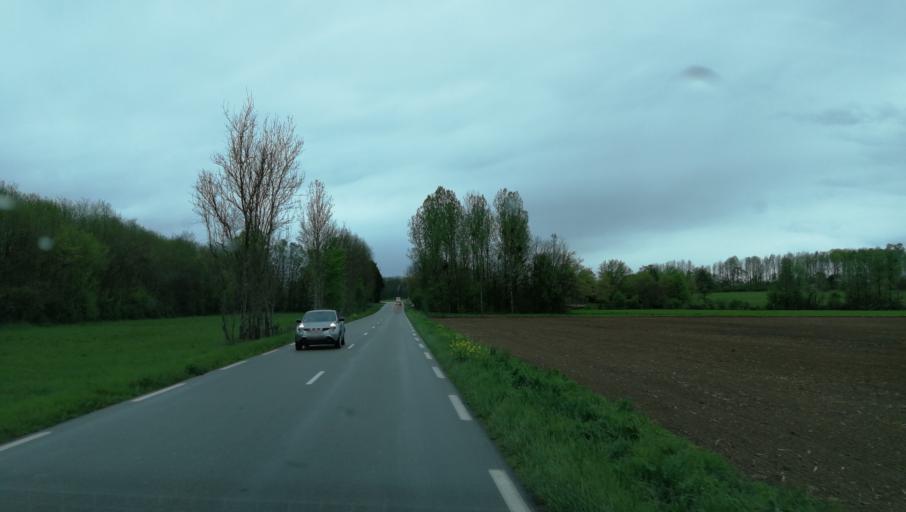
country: FR
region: Franche-Comte
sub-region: Departement du Jura
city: Bletterans
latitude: 46.7205
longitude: 5.4735
